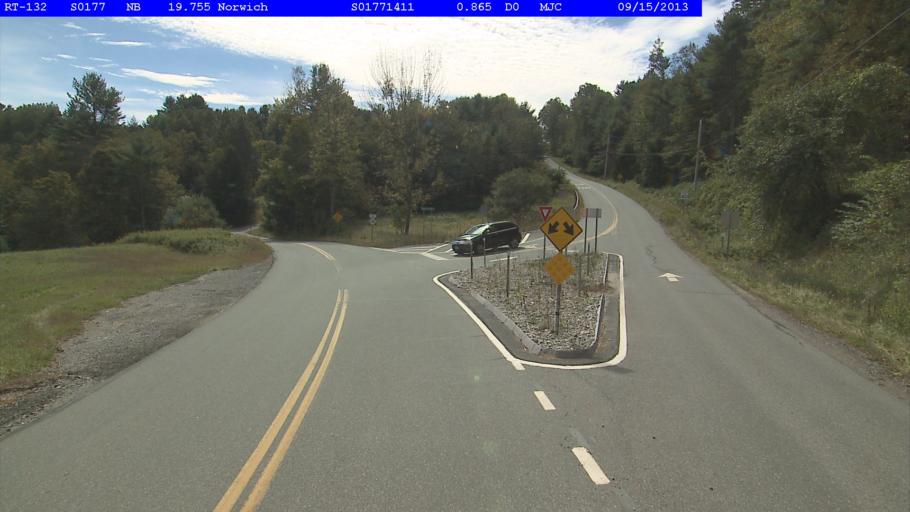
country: US
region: New Hampshire
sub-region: Grafton County
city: Hanover
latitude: 43.7743
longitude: -72.2579
